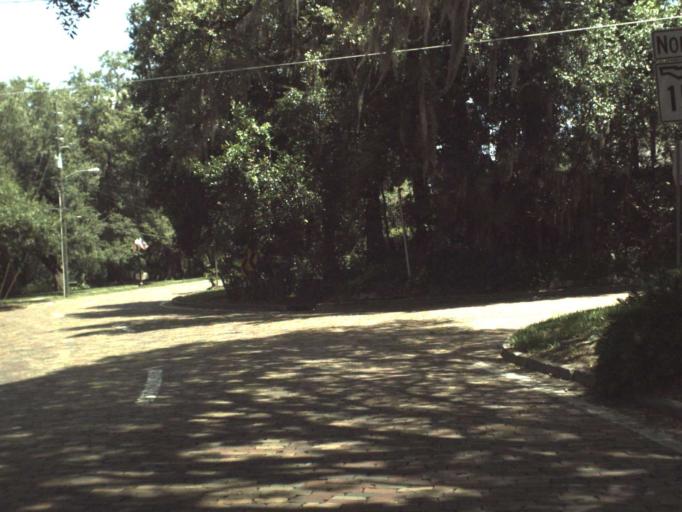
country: US
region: Florida
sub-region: Orange County
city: Orlando
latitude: 28.5401
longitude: -81.3630
